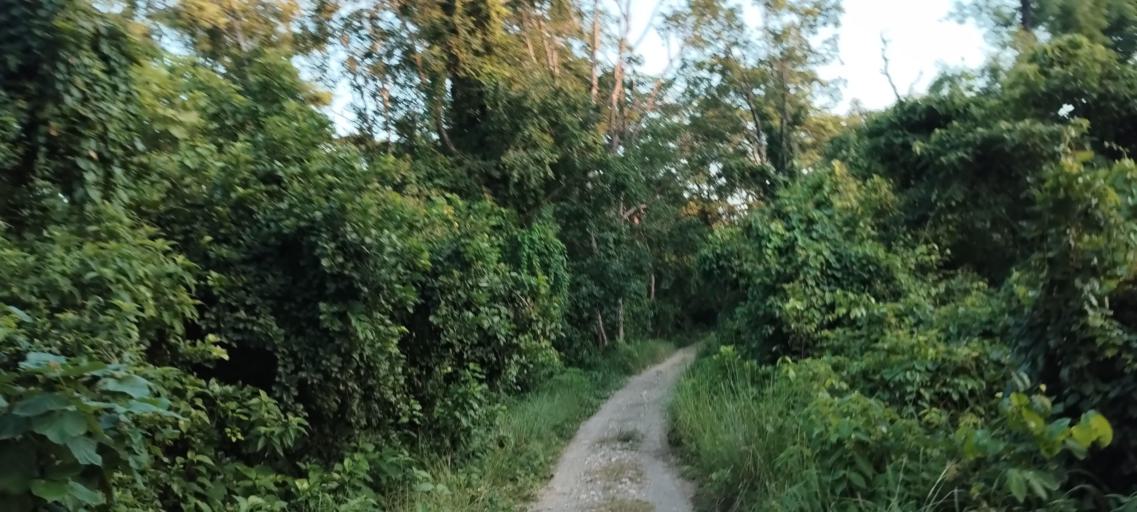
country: NP
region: Far Western
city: Tikapur
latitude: 28.4578
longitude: 81.2422
